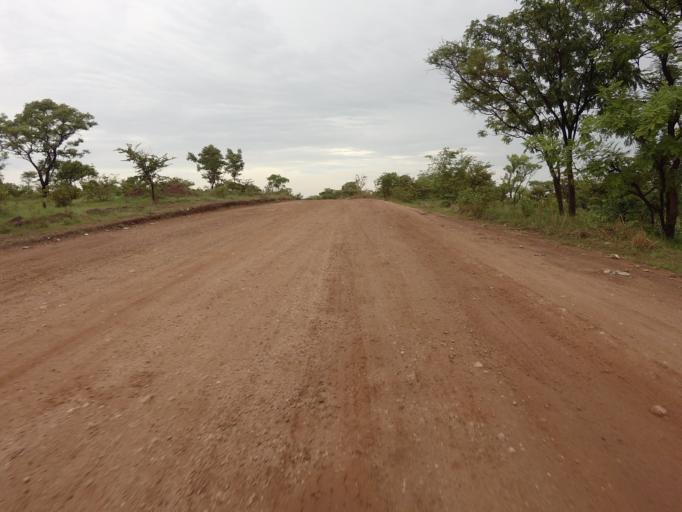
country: GH
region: Upper East
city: Bolgatanga
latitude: 10.8739
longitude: -0.6398
